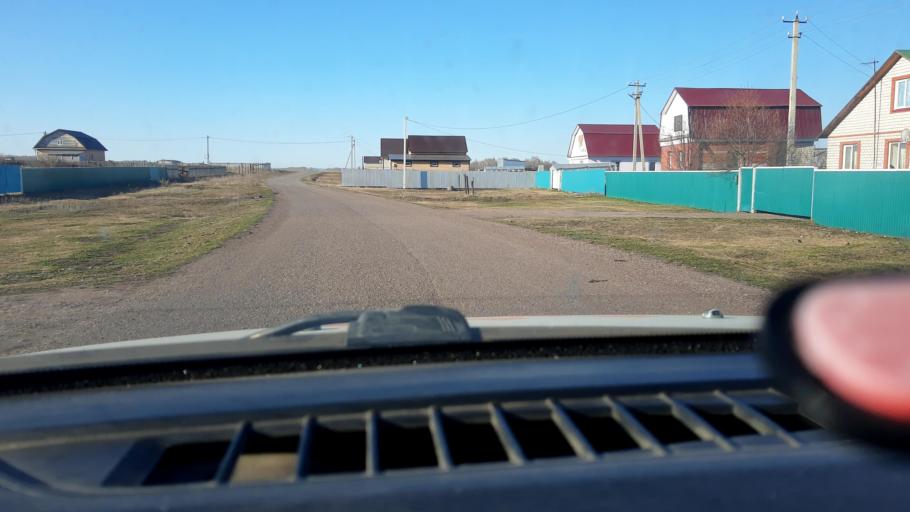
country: RU
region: Bashkortostan
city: Asanovo
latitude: 54.9050
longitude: 55.4853
